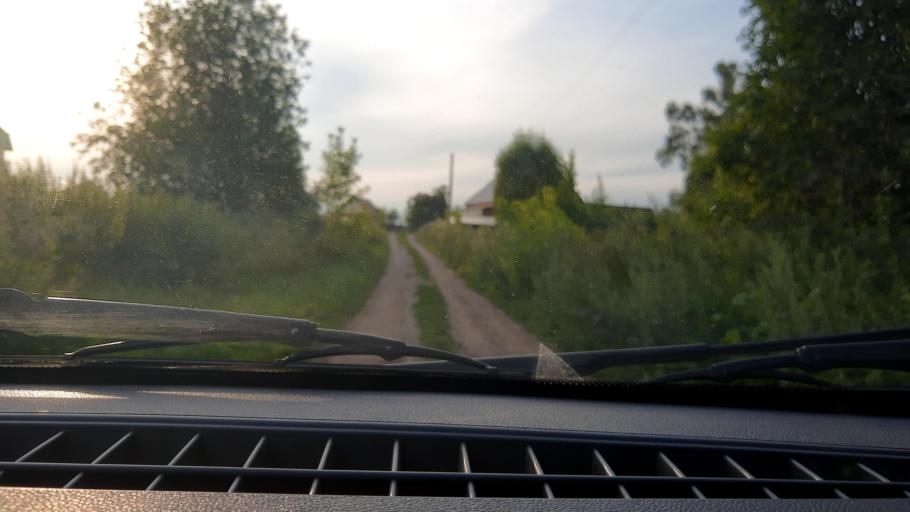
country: RU
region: Bashkortostan
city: Mikhaylovka
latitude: 54.8138
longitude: 55.8491
